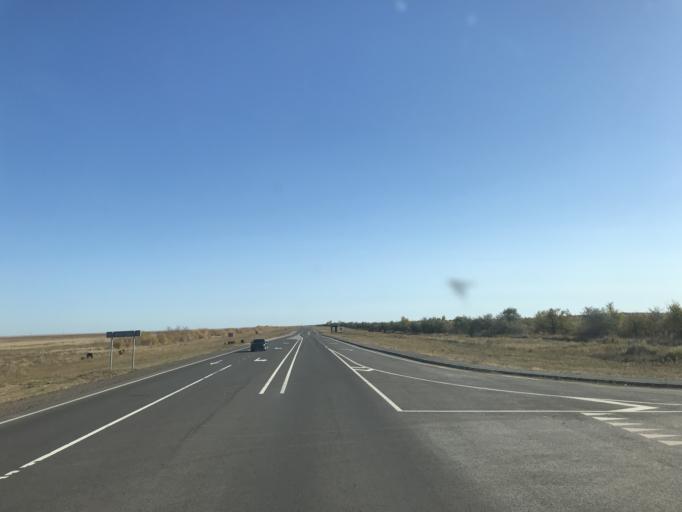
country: KZ
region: Pavlodar
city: Aksu
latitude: 52.0635
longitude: 77.1641
